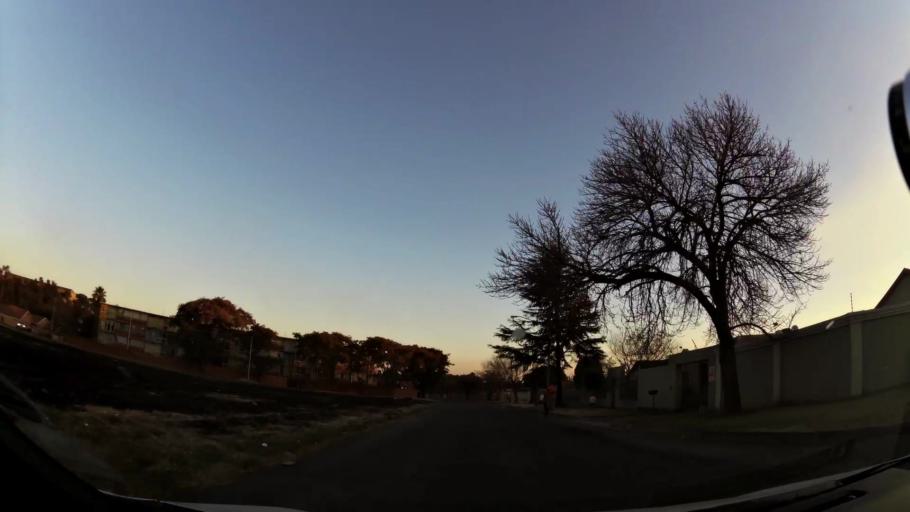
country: ZA
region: Gauteng
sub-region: Ekurhuleni Metropolitan Municipality
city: Germiston
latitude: -26.2719
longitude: 28.1568
